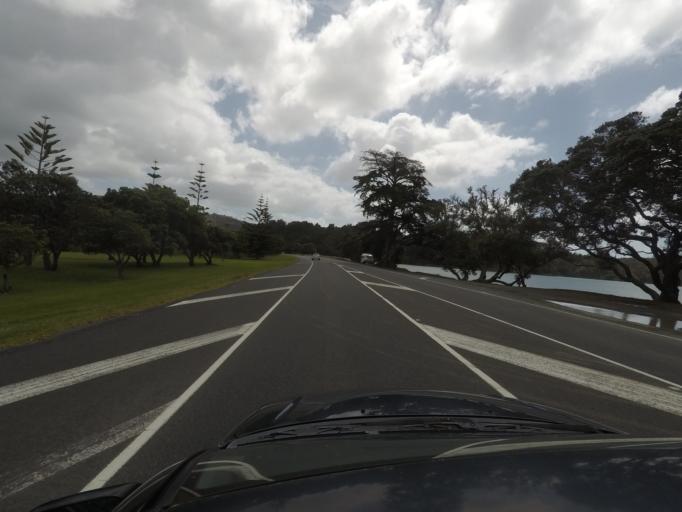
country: NZ
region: Auckland
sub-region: Auckland
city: Warkworth
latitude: -36.5649
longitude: 174.6949
